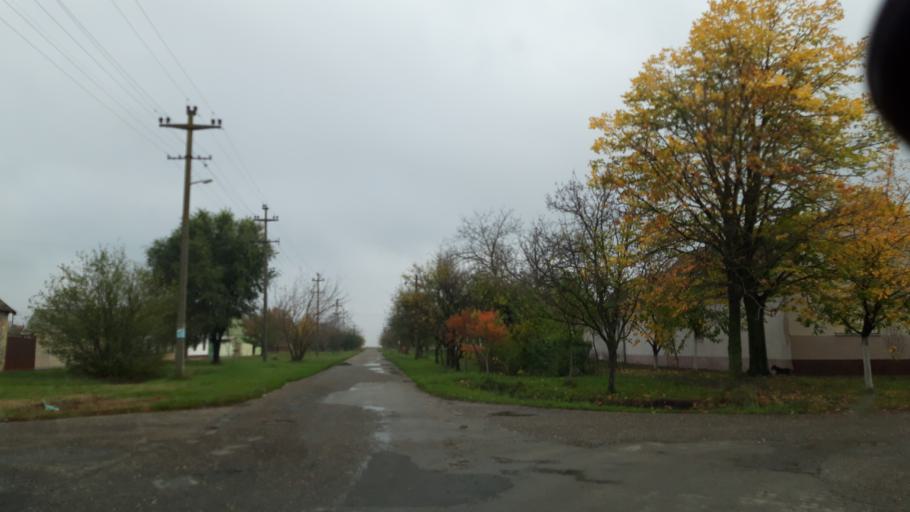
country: RS
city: Backo Gradiste
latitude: 45.5094
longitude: 19.9291
